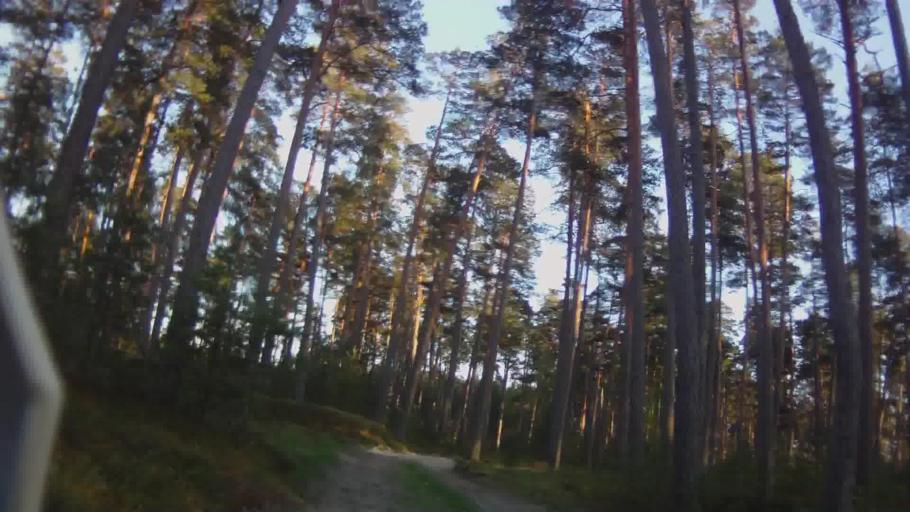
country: LV
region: Riga
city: Jaunciems
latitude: 57.0644
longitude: 24.1713
